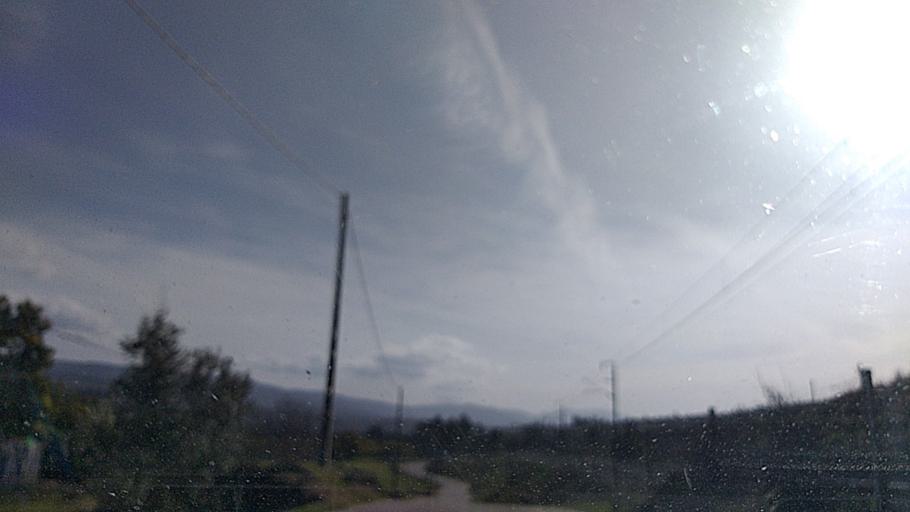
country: PT
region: Guarda
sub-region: Celorico da Beira
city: Celorico da Beira
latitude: 40.6367
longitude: -7.4329
